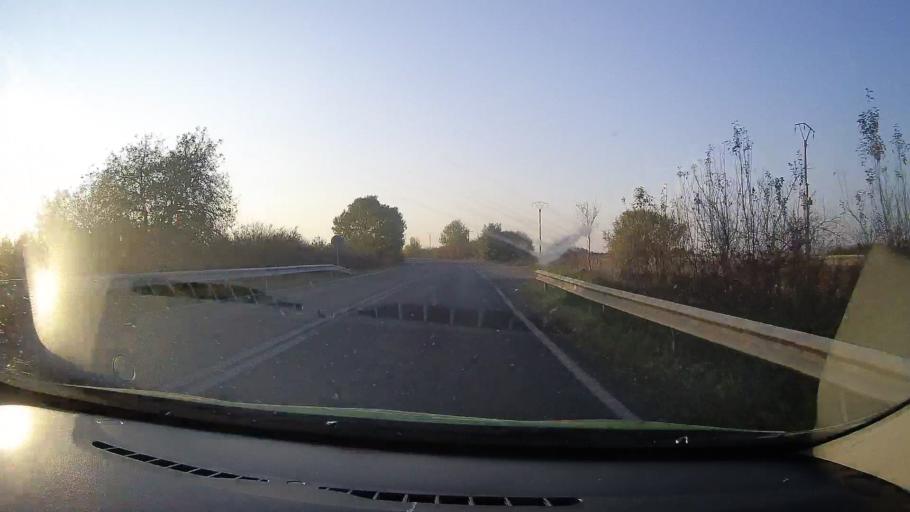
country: RO
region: Arad
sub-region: Comuna Barsa
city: Barsa
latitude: 46.3915
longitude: 22.0509
